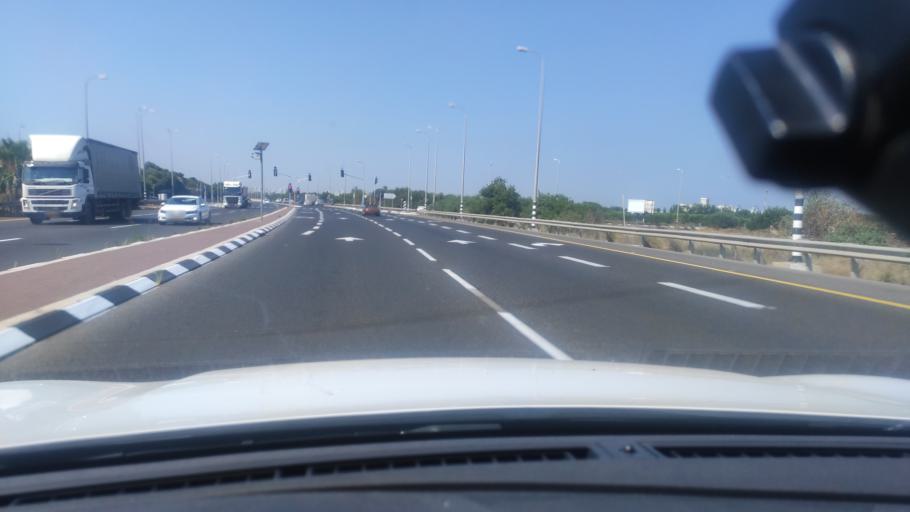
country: IL
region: Central District
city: Kfar Saba
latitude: 32.1526
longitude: 34.9219
